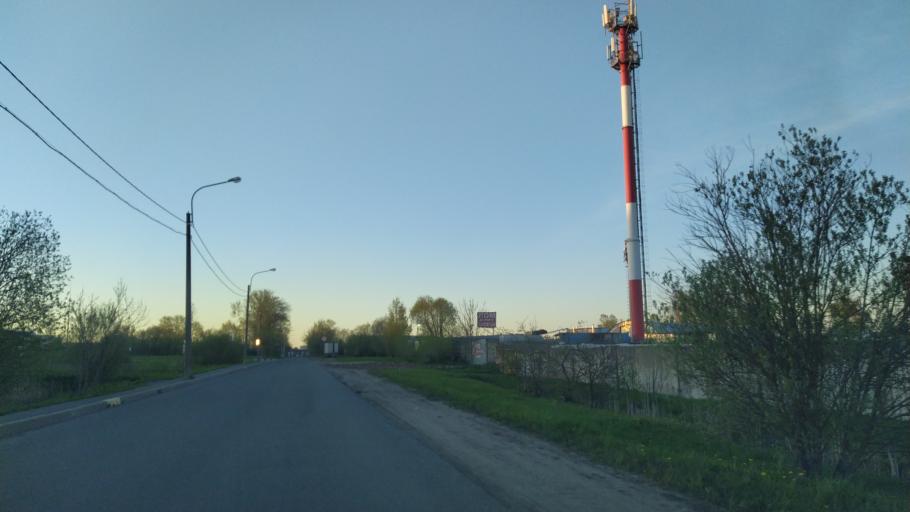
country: RU
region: St.-Petersburg
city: Pushkin
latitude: 59.6965
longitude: 30.3904
